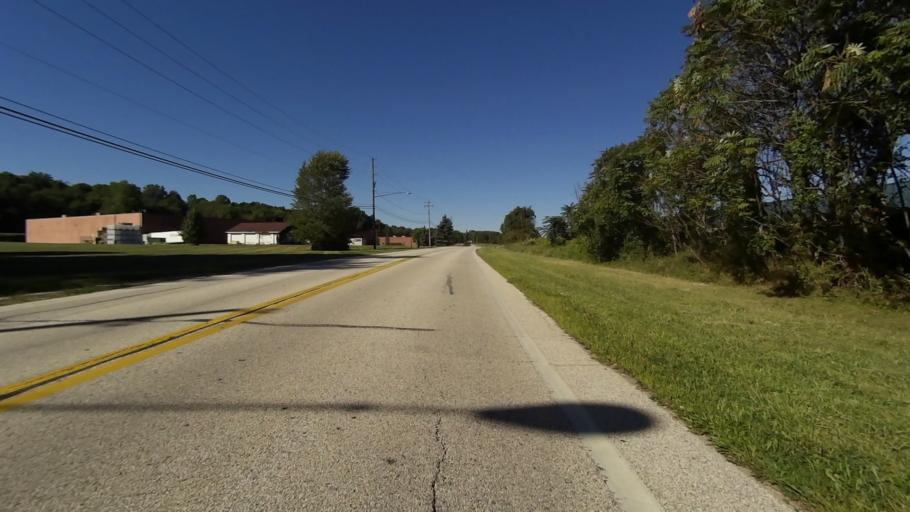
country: US
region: Ohio
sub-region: Portage County
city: Kent
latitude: 41.1377
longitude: -81.3798
